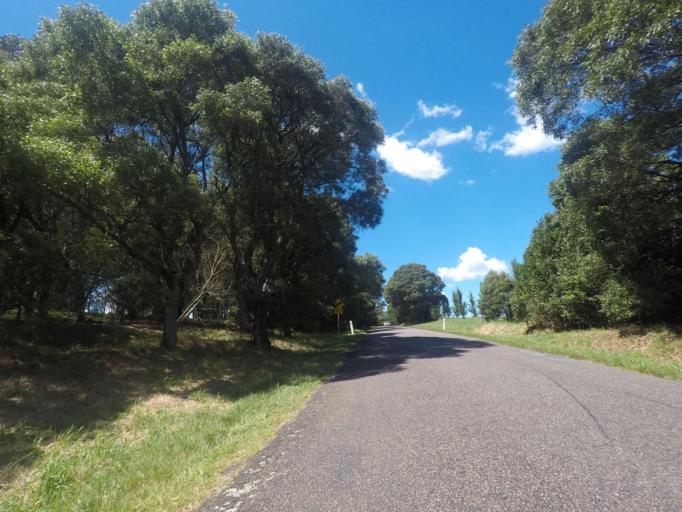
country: AU
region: New South Wales
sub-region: Shellharbour
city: Calderwood
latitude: -34.5692
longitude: 150.5921
